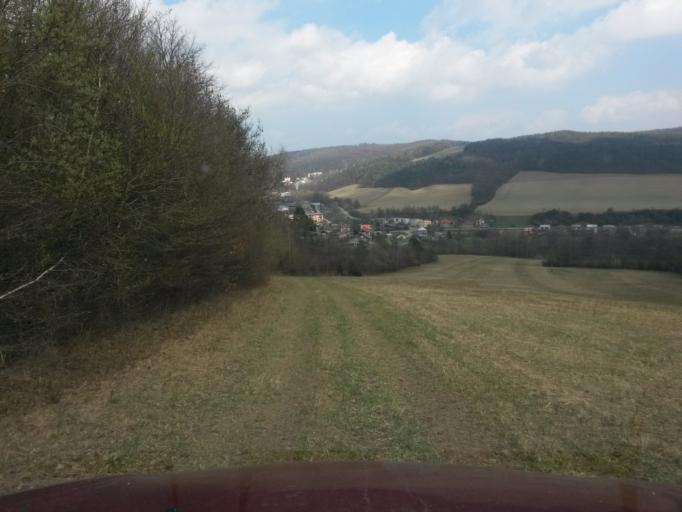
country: SK
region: Presovsky
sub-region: Okres Presov
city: Presov
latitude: 48.9415
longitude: 21.1646
